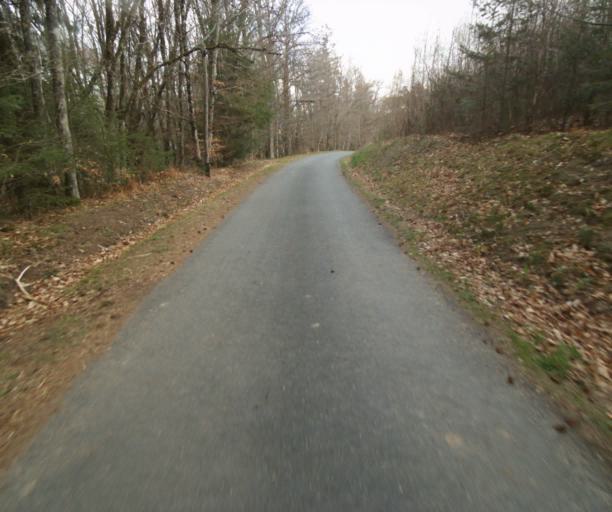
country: FR
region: Limousin
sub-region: Departement de la Correze
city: Correze
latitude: 45.2765
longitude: 1.9509
